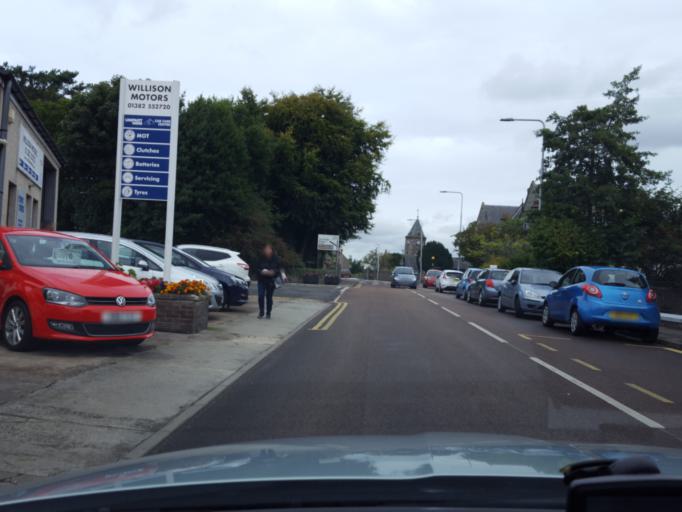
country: GB
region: Scotland
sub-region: Fife
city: Tayport
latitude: 56.4461
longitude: -2.8804
